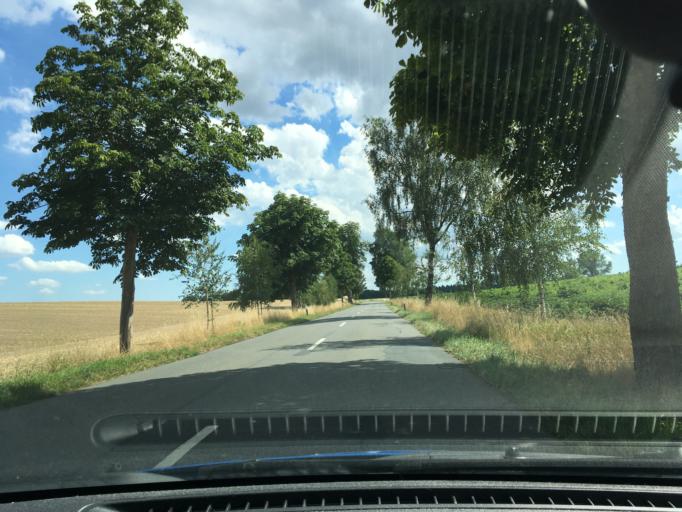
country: DE
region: Lower Saxony
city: Rehlingen
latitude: 53.0603
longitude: 10.2378
